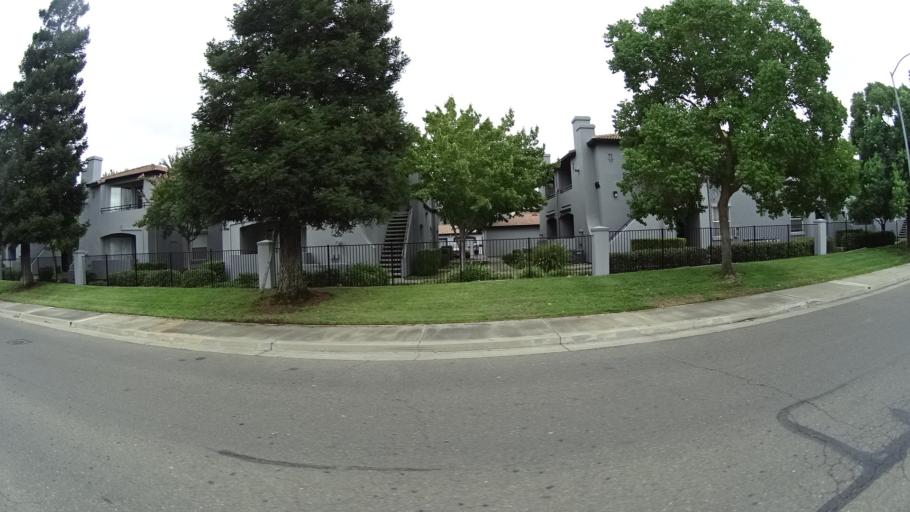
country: US
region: California
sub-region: Sacramento County
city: Laguna
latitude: 38.4227
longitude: -121.4445
